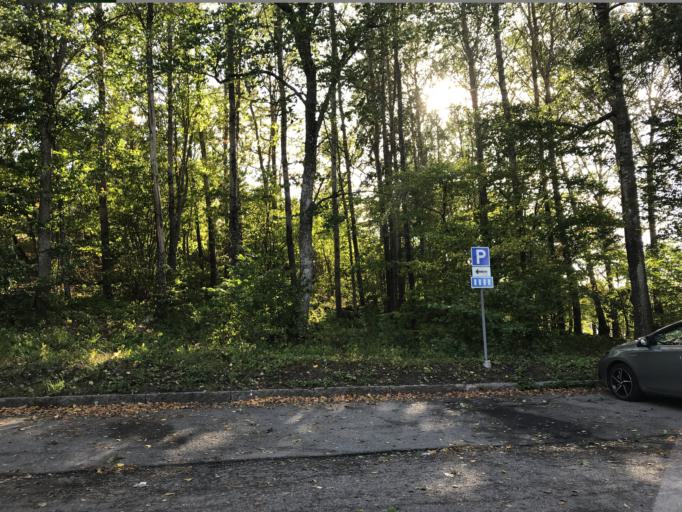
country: SE
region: Stockholm
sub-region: Huddinge Kommun
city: Segeltorp
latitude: 59.2858
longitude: 17.8918
